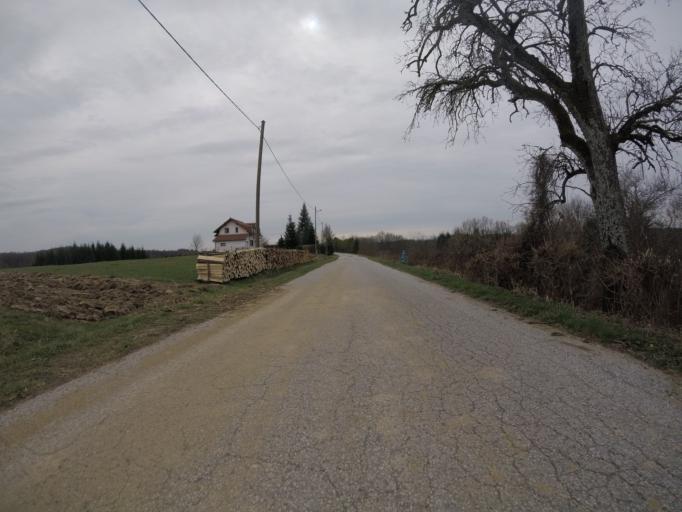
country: HR
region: Zagrebacka
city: Lukavec
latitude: 45.5656
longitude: 15.9750
